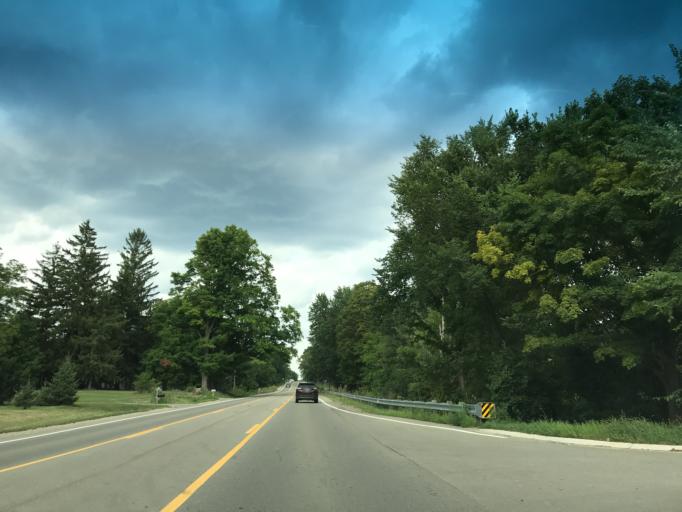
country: US
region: Michigan
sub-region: Oakland County
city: Milford
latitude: 42.5403
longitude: -83.6172
